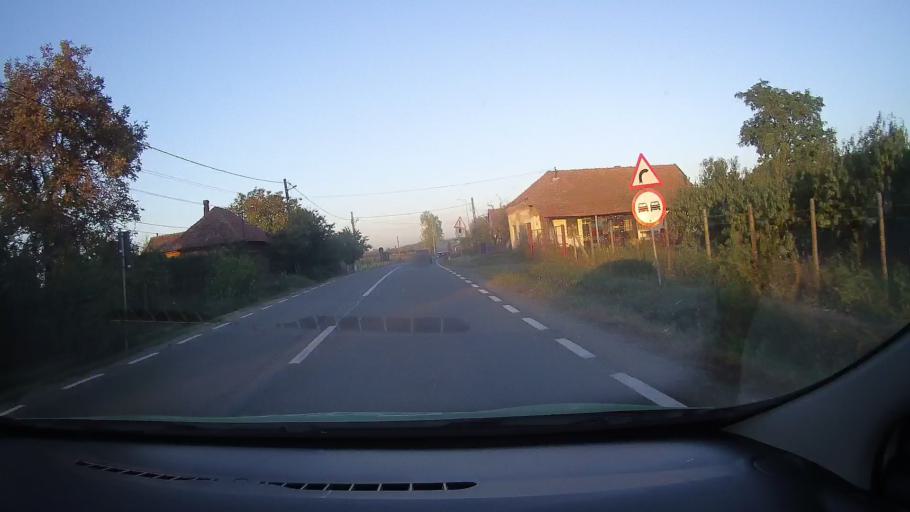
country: RO
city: Dioszeg
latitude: 47.2862
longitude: 21.9939
